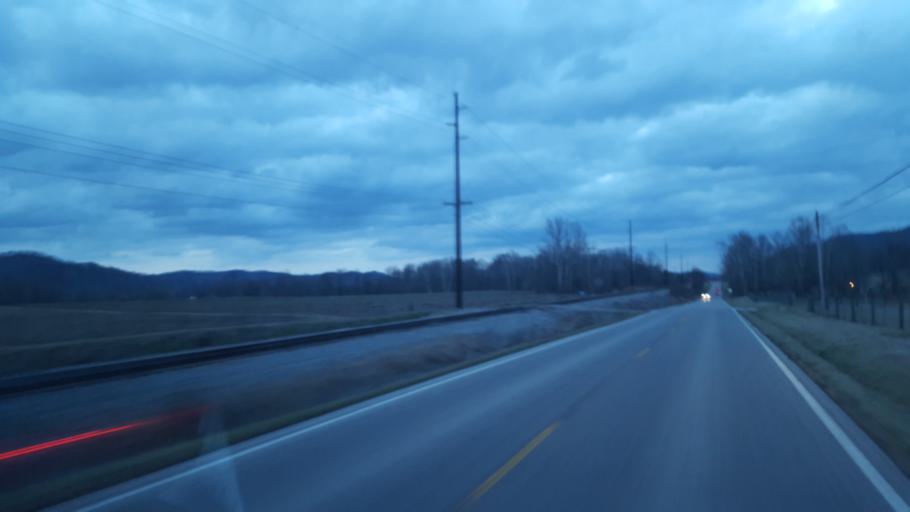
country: US
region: Ohio
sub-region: Scioto County
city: West Portsmouth
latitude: 38.6307
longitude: -83.1254
